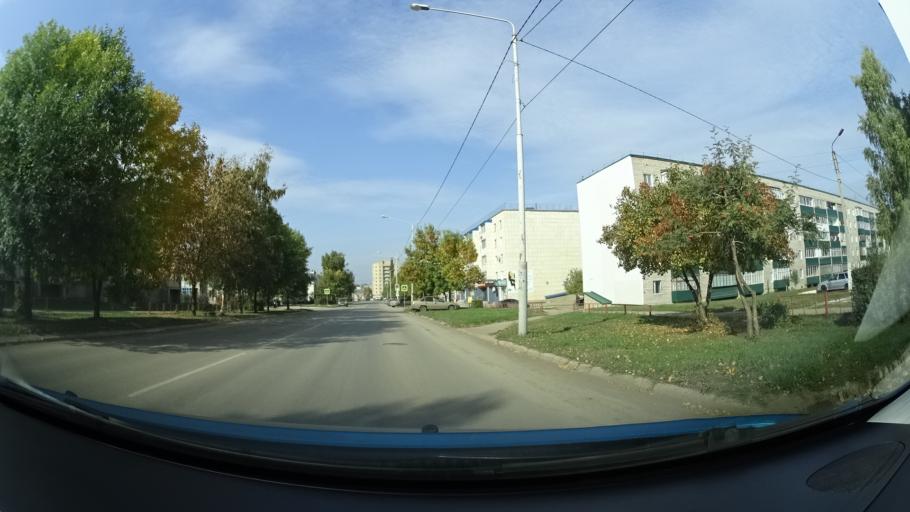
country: RU
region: Bashkortostan
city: Tuymazy
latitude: 54.6049
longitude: 53.6967
